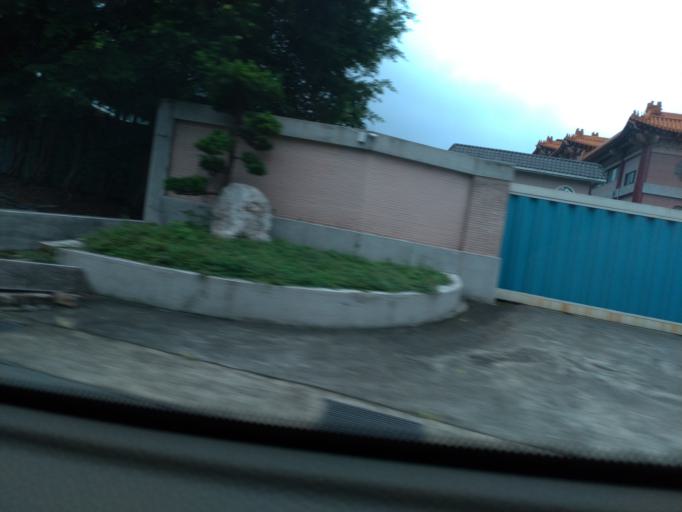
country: TW
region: Taipei
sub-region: Taipei
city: Banqiao
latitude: 24.9309
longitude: 121.4096
